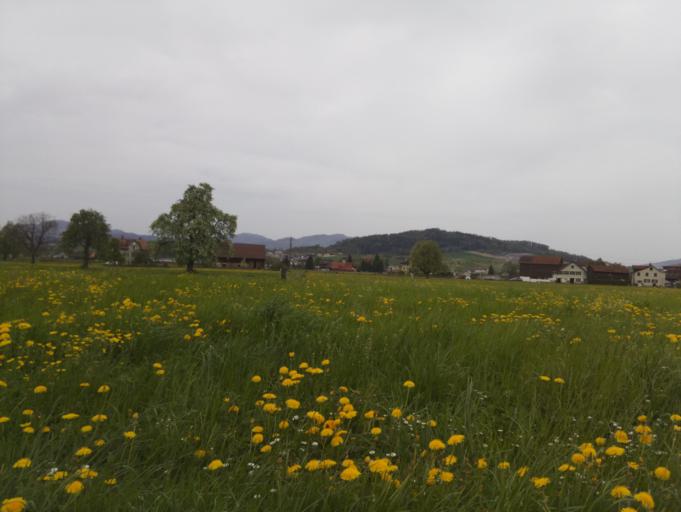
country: CH
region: Schwyz
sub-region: Bezirk March
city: Lachen
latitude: 47.1813
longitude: 8.8872
